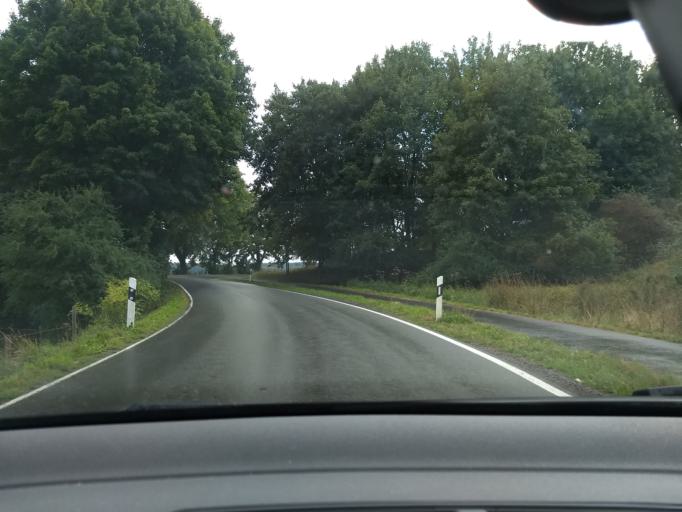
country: DE
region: North Rhine-Westphalia
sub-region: Regierungsbezirk Arnsberg
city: Finnentrop
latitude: 51.1895
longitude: 8.0191
